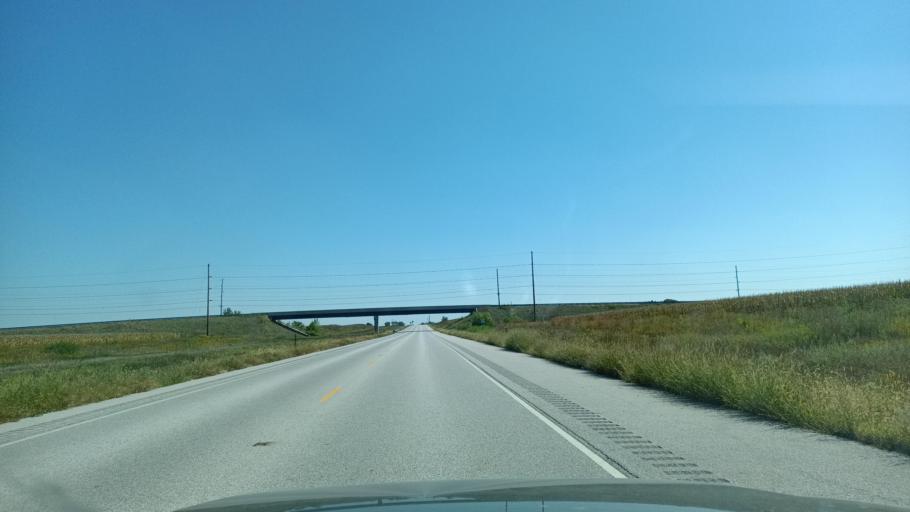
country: US
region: Illinois
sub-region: McDonough County
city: Macomb
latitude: 40.5033
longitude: -90.6973
